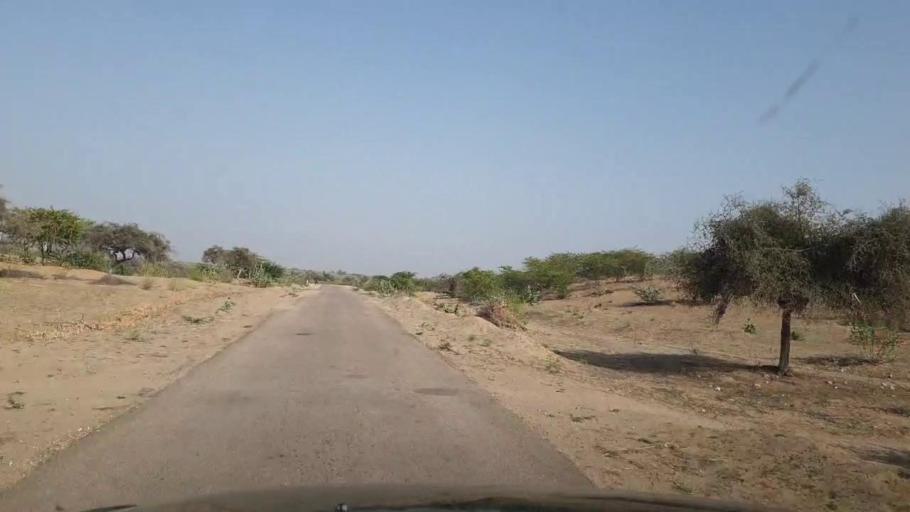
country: PK
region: Sindh
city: Islamkot
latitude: 25.1239
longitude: 70.5120
